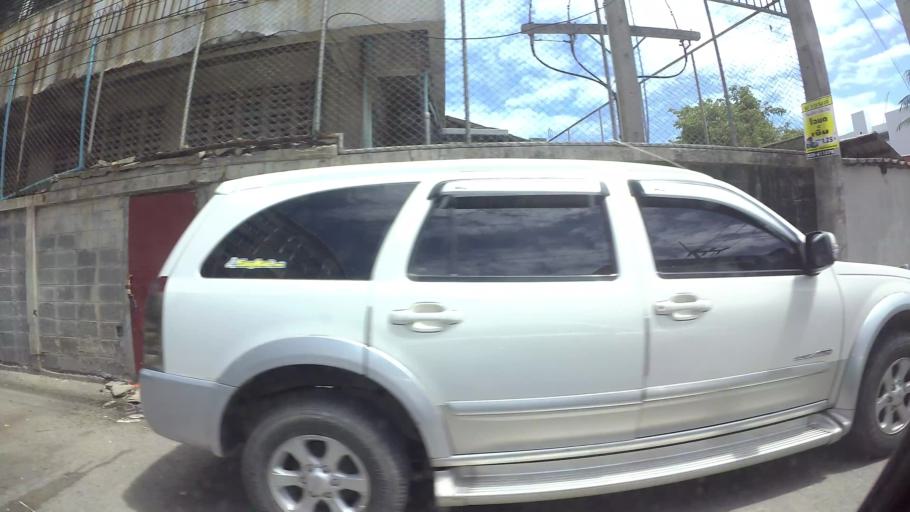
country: TH
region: Chon Buri
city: Phatthaya
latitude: 12.9280
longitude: 100.8805
